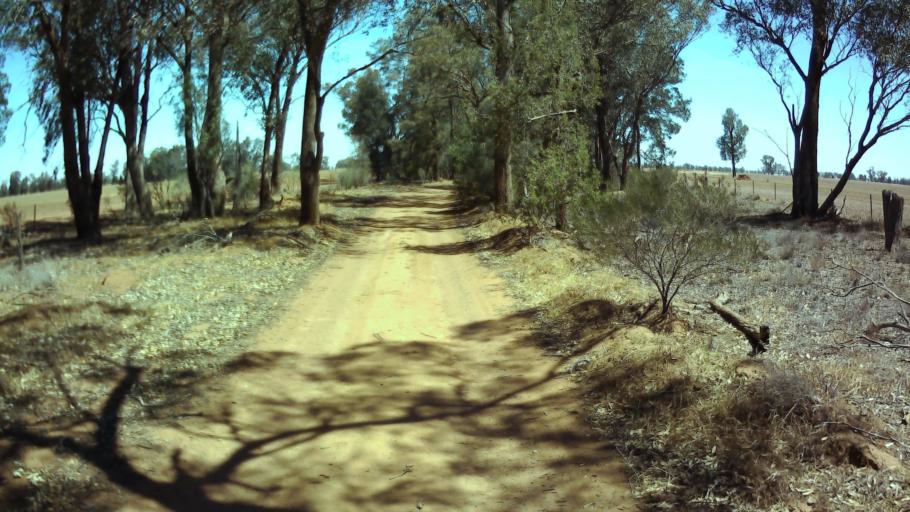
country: AU
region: New South Wales
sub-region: Bland
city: West Wyalong
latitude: -33.9188
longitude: 147.6830
